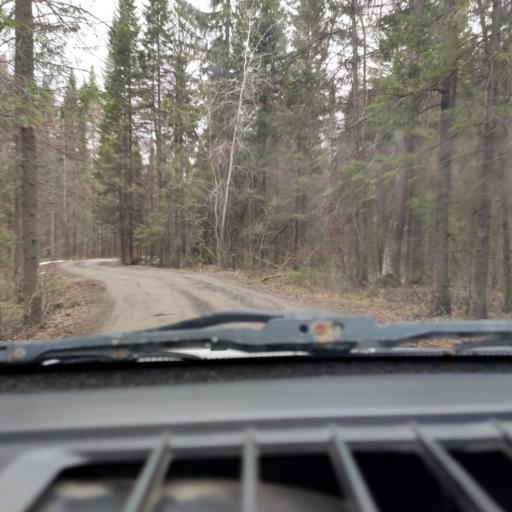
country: RU
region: Perm
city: Kultayevo
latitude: 57.8224
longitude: 55.7946
